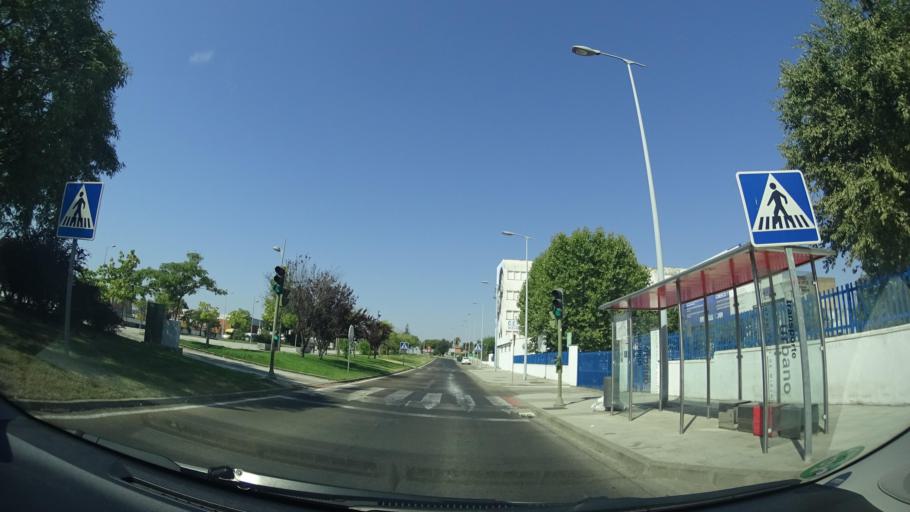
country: ES
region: Extremadura
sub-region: Provincia de Caceres
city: Miajadas
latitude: 39.1446
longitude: -5.9232
